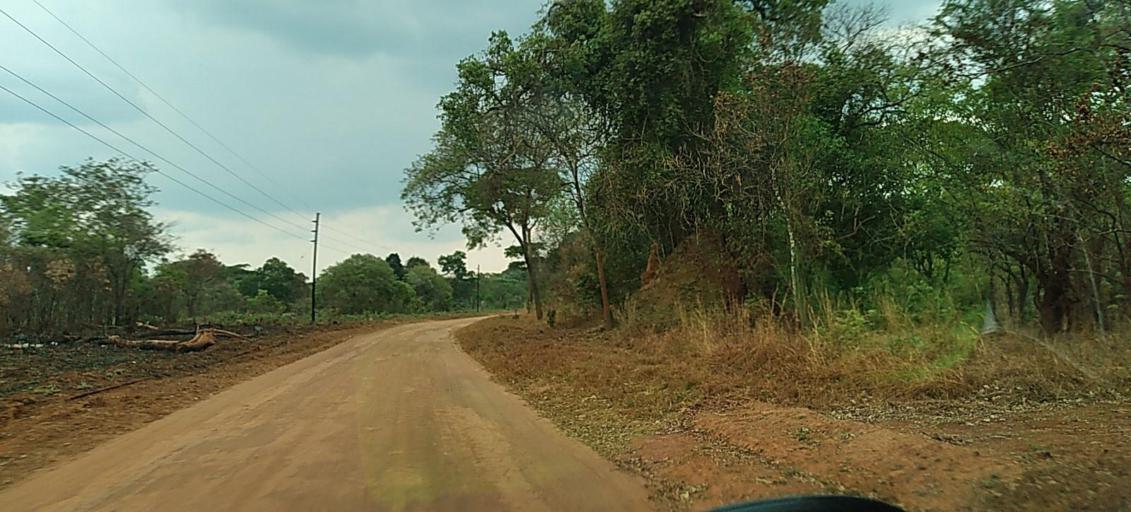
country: ZM
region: North-Western
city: Solwezi
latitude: -12.7807
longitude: 26.4813
